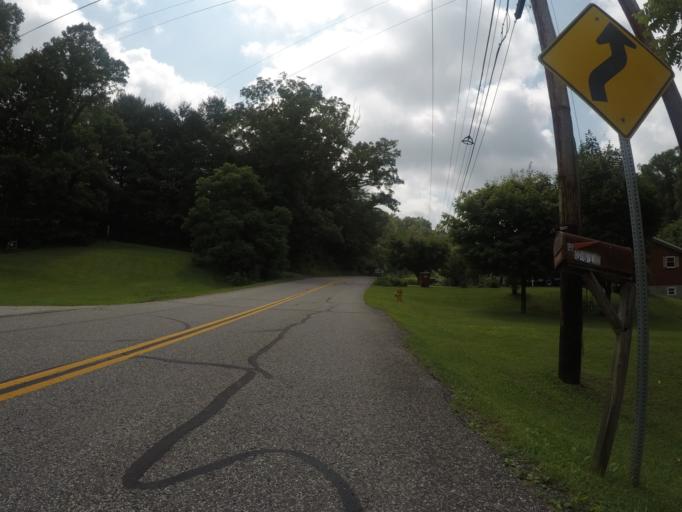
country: US
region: Kentucky
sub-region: Boyd County
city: Meads
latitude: 38.4065
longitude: -82.6614
